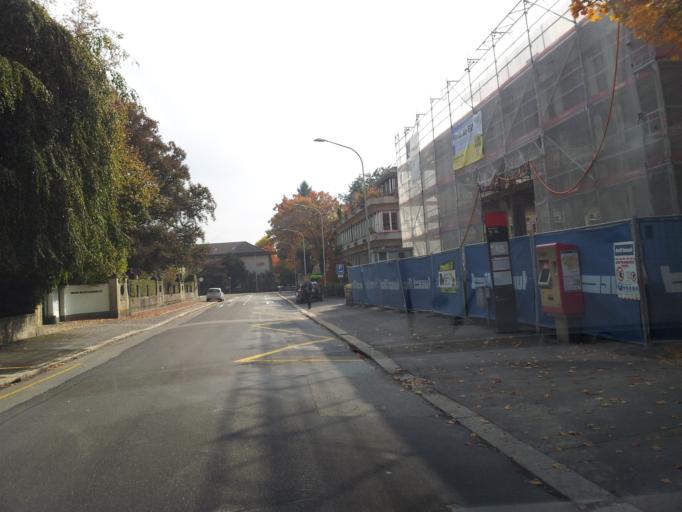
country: CH
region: Bern
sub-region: Bern-Mittelland District
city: Bern
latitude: 46.9394
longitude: 7.4617
